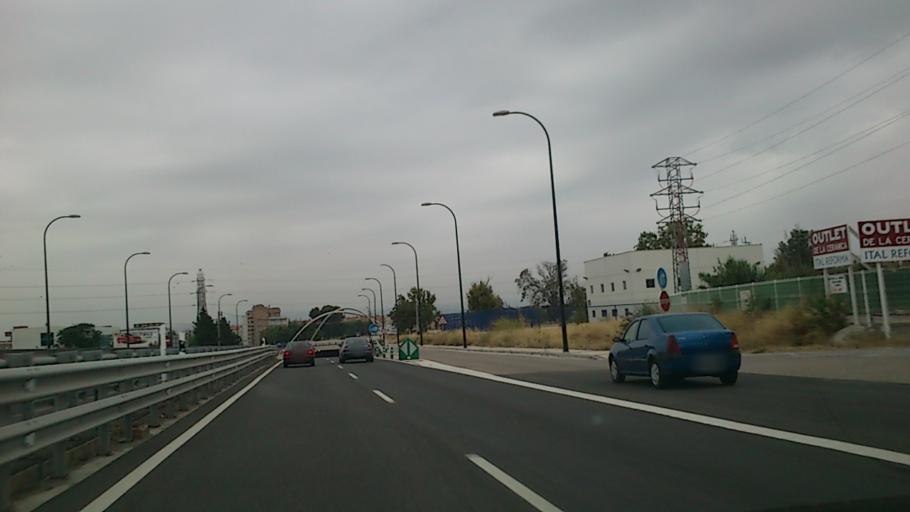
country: ES
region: Aragon
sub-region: Provincia de Zaragoza
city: Zaragoza
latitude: 41.6933
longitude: -0.8701
